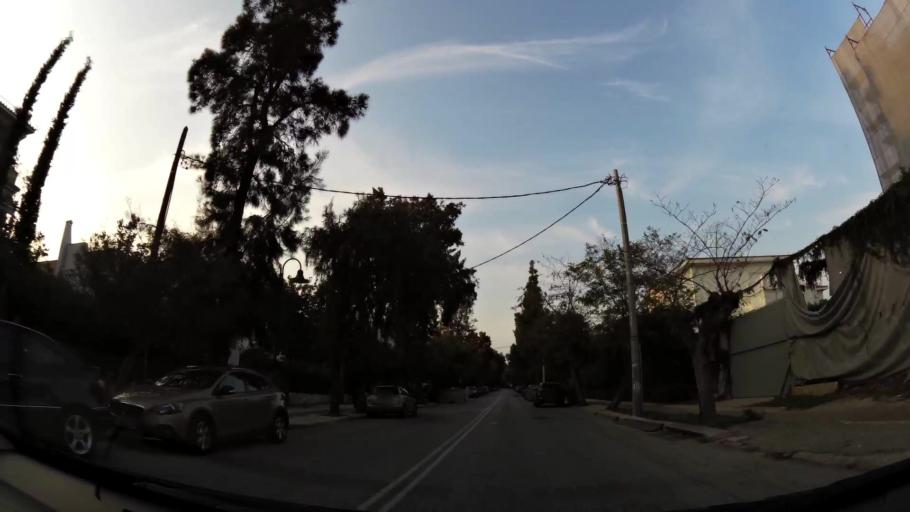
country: GR
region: Attica
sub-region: Nomarchia Athinas
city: Psychiko
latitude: 38.0111
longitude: 23.7730
